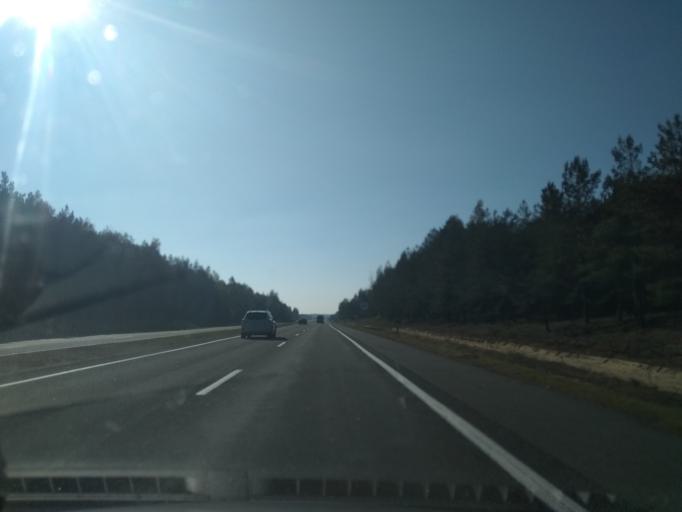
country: BY
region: Brest
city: Ivatsevichy
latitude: 52.7976
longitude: 25.5654
